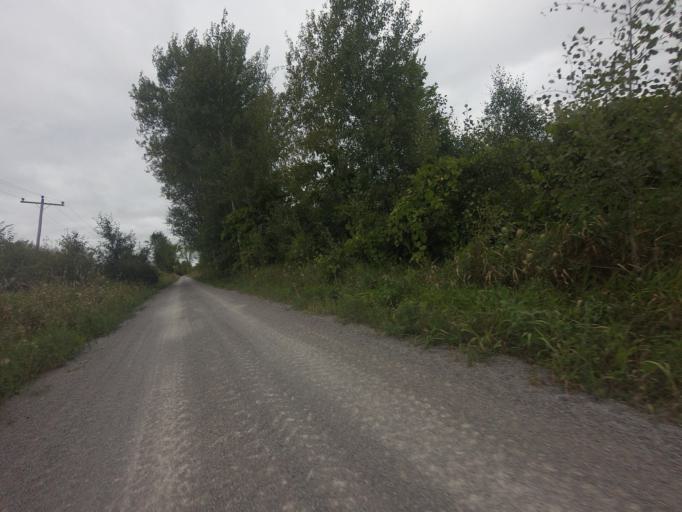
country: CA
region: Ontario
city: Omemee
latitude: 44.4620
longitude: -78.7574
